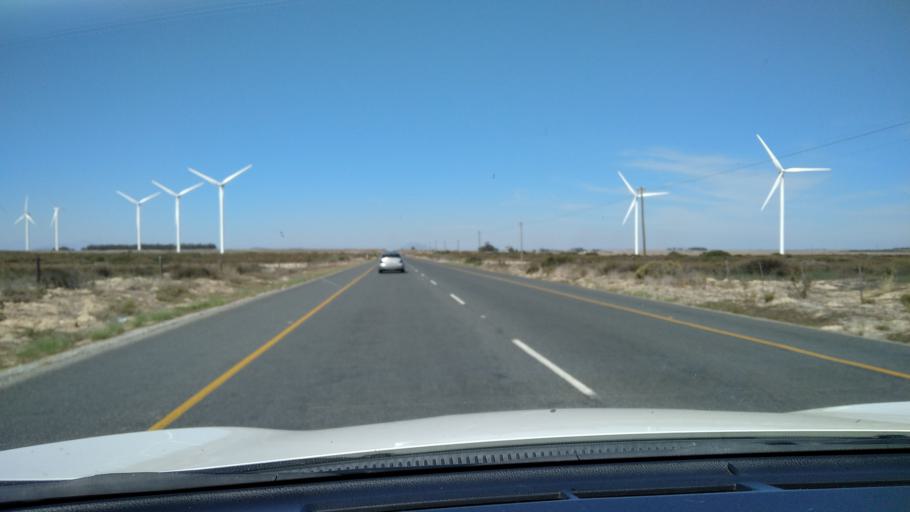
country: ZA
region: Western Cape
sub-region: West Coast District Municipality
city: Moorreesburg
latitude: -33.0871
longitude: 18.4006
